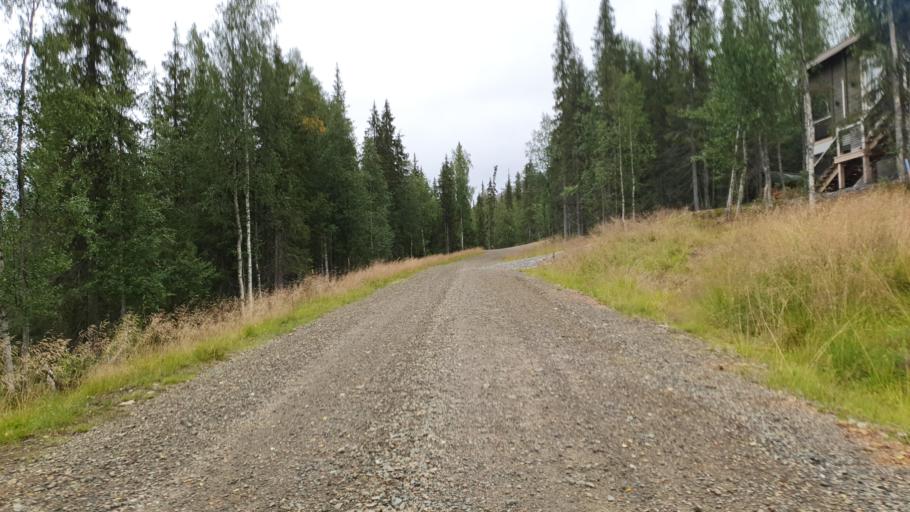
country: FI
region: Lapland
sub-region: Tunturi-Lappi
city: Kolari
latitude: 67.5990
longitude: 24.2007
